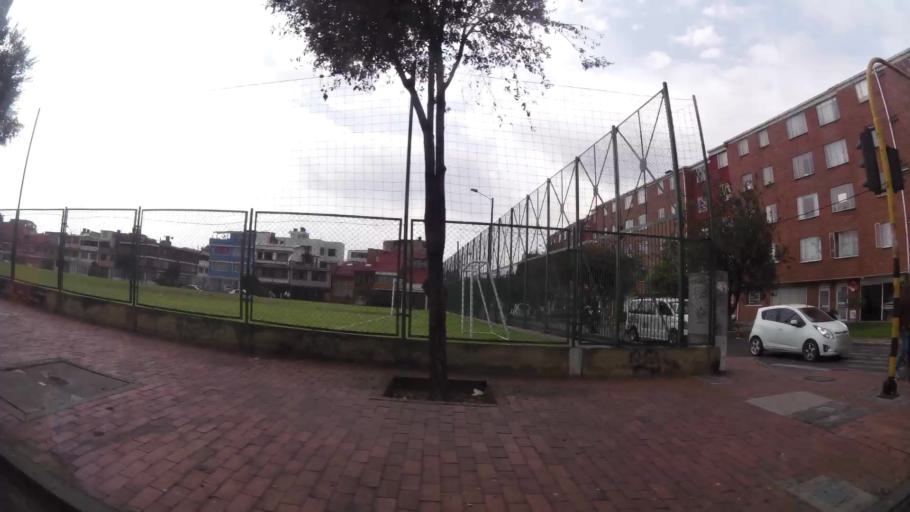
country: CO
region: Bogota D.C.
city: Bogota
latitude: 4.6070
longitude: -74.1081
